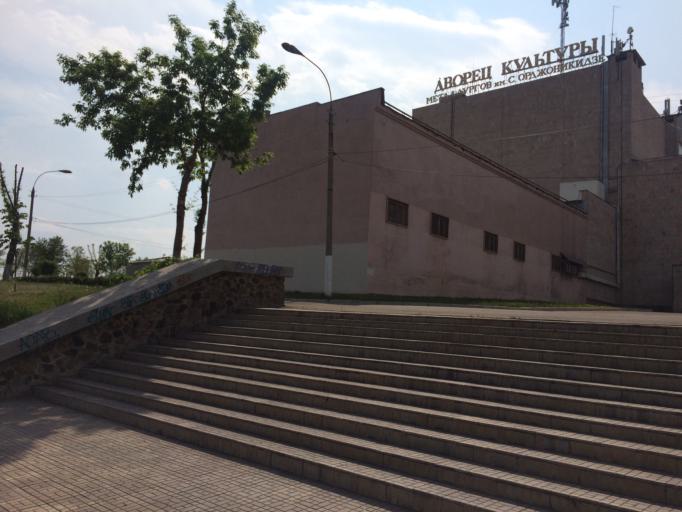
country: RU
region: Chelyabinsk
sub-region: Gorod Magnitogorsk
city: Magnitogorsk
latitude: 53.4181
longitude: 59.0040
